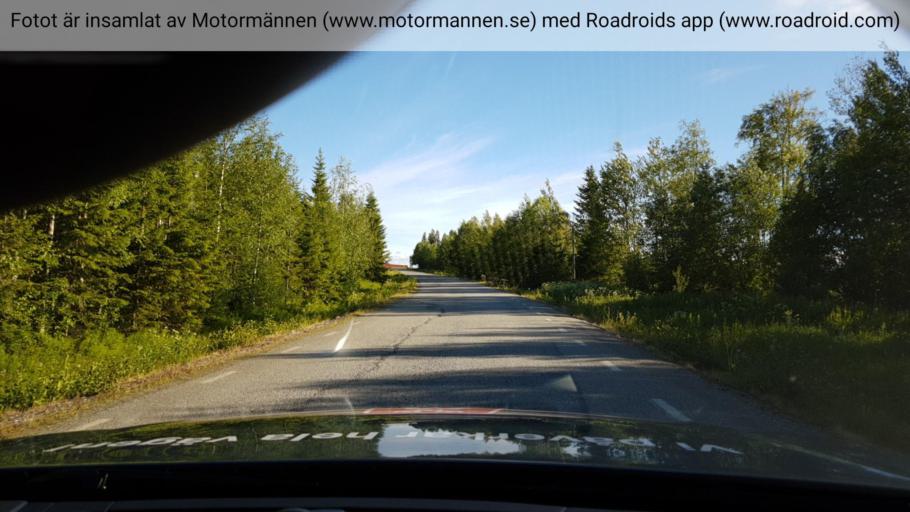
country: SE
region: Jaemtland
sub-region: Bergs Kommun
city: Hoverberg
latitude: 62.9317
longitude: 14.3692
